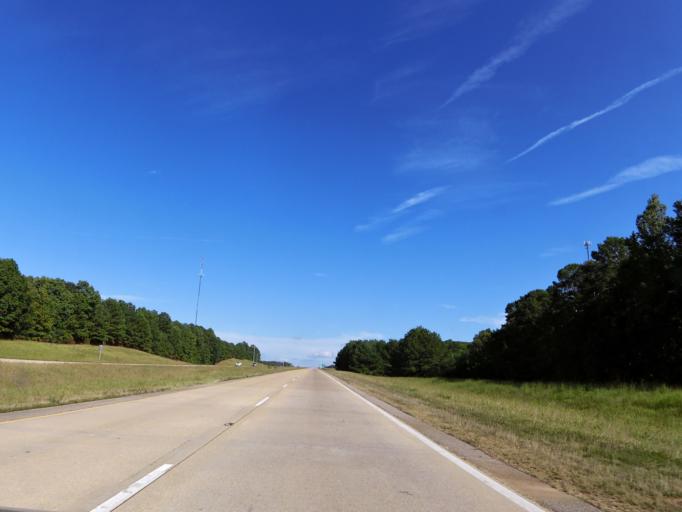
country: US
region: Mississippi
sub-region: Tishomingo County
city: Iuka
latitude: 34.7970
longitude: -88.2191
